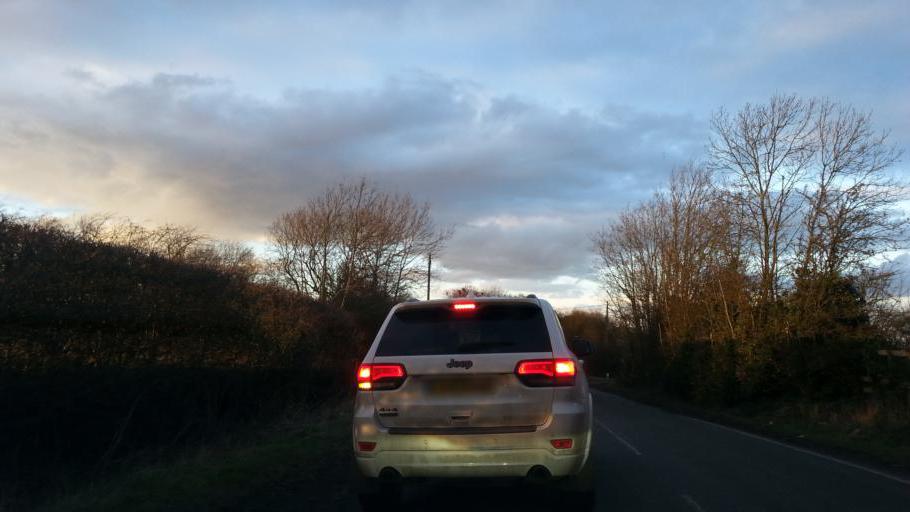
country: GB
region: England
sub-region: Nottinghamshire
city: Southwell
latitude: 53.1270
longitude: -0.8863
